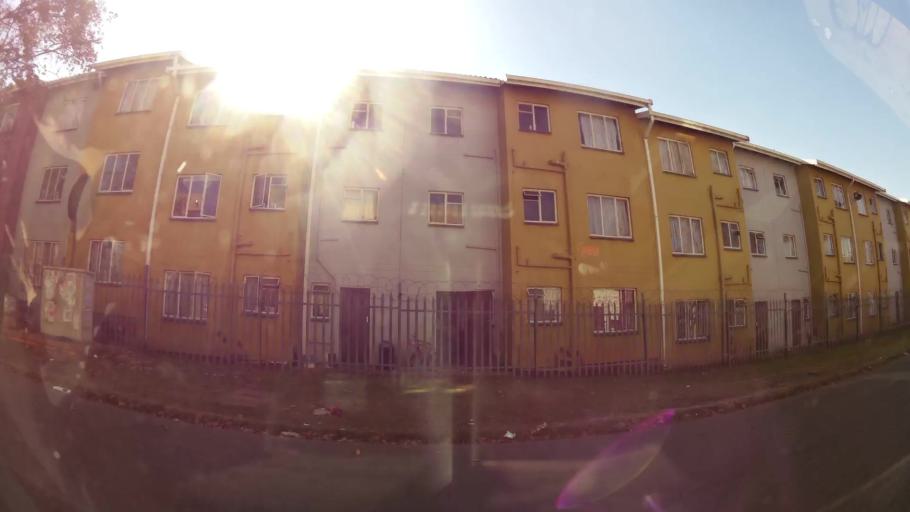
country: ZA
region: Gauteng
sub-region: City of Johannesburg Metropolitan Municipality
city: Johannesburg
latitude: -26.2022
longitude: 28.0246
